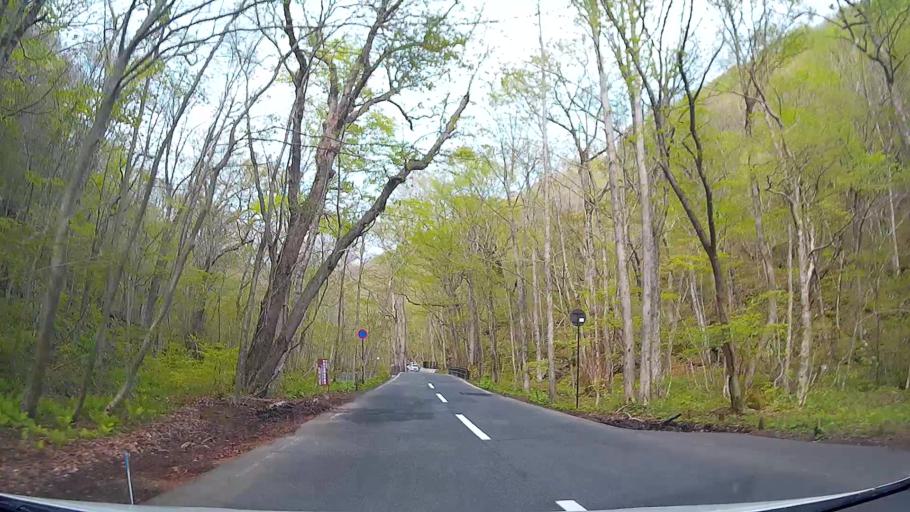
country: JP
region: Akita
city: Hanawa
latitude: 40.4864
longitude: 140.9484
